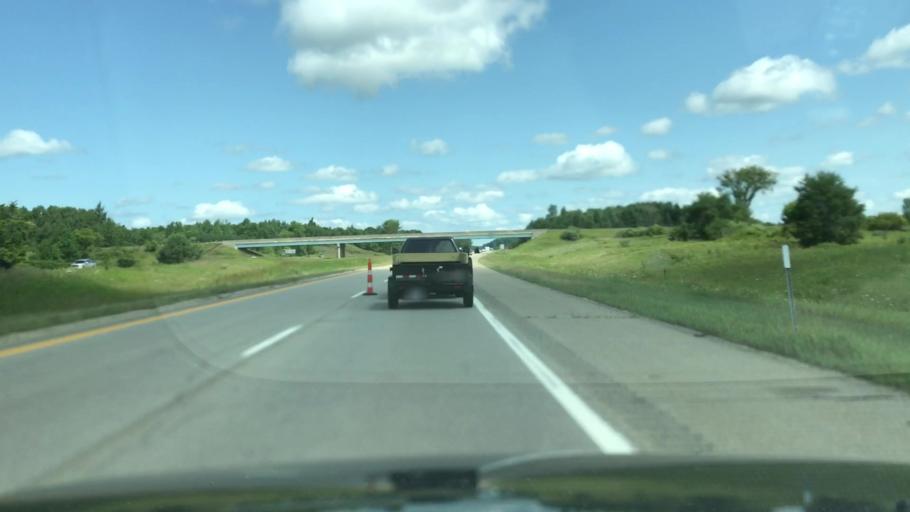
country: US
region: Michigan
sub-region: Mecosta County
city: Big Rapids
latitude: 43.7690
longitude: -85.5345
